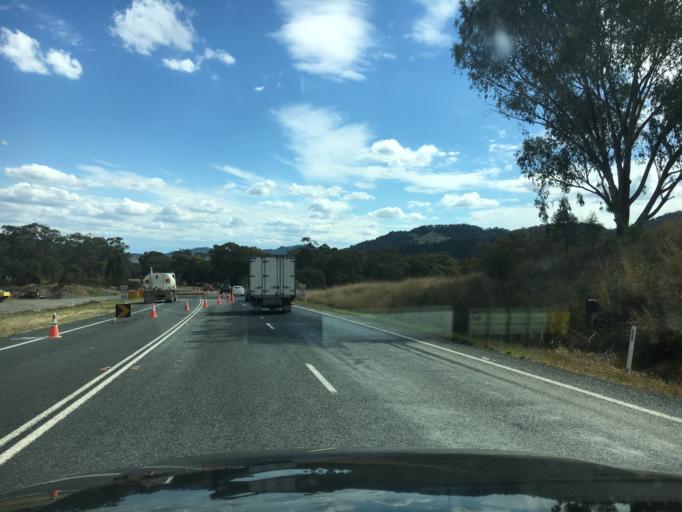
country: AU
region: New South Wales
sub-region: Liverpool Plains
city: Quirindi
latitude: -31.4508
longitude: 150.8639
